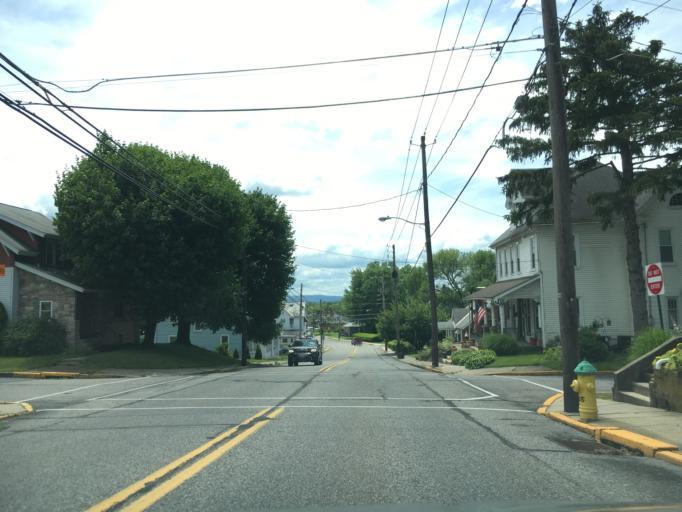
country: US
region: Pennsylvania
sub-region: Lehigh County
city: Cementon
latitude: 40.7021
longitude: -75.5050
